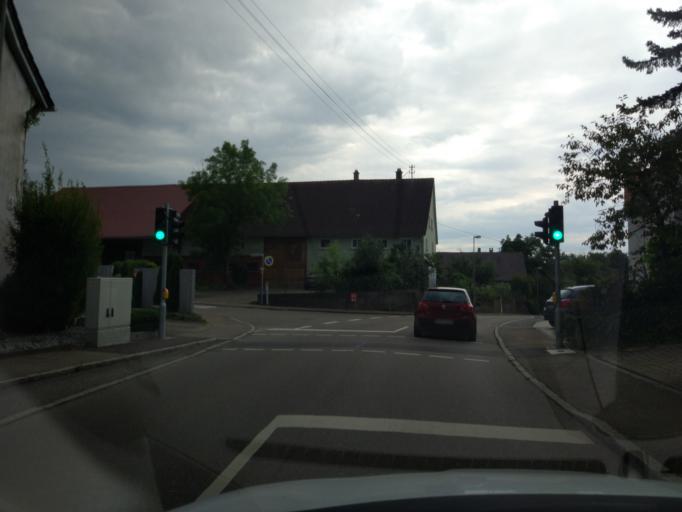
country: DE
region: Baden-Wuerttemberg
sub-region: Tuebingen Region
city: Erbach
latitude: 48.3385
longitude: 9.9391
